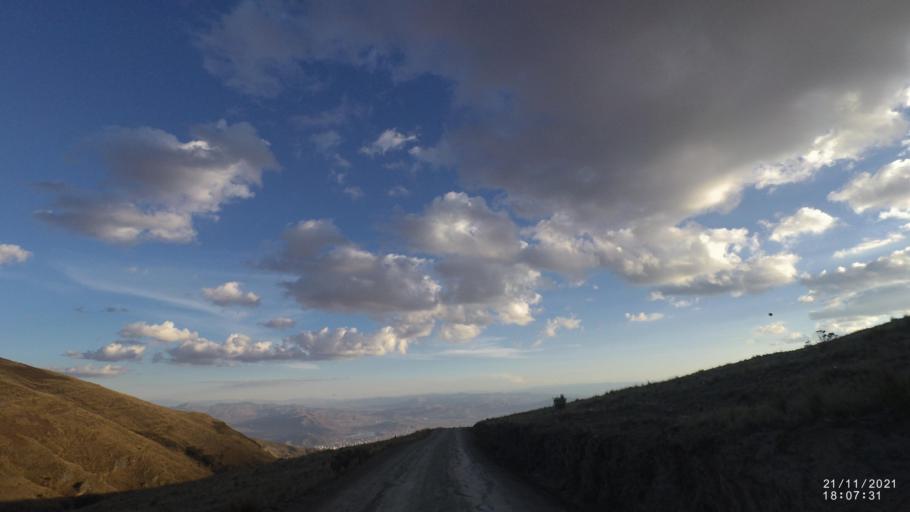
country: BO
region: Cochabamba
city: Cochabamba
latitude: -17.2783
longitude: -66.2105
